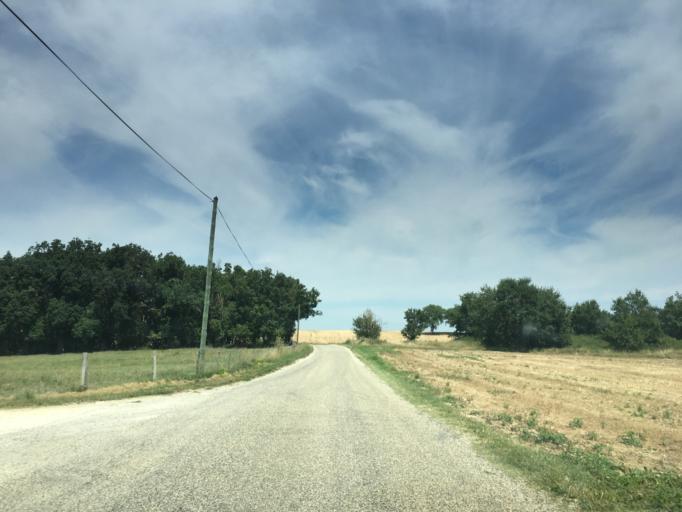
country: FR
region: Midi-Pyrenees
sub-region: Departement du Gers
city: Jegun
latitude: 43.8002
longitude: 0.4974
